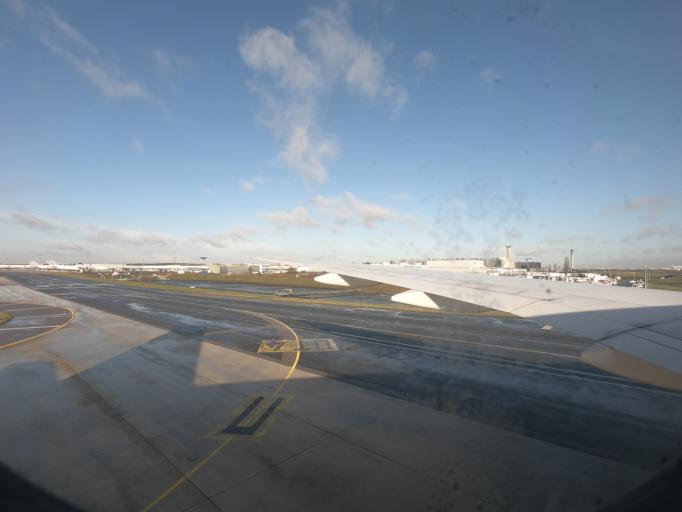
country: FR
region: Ile-de-France
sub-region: Departement du Val-d'Oise
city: Roissy-en-France
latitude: 48.9995
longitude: 2.5538
